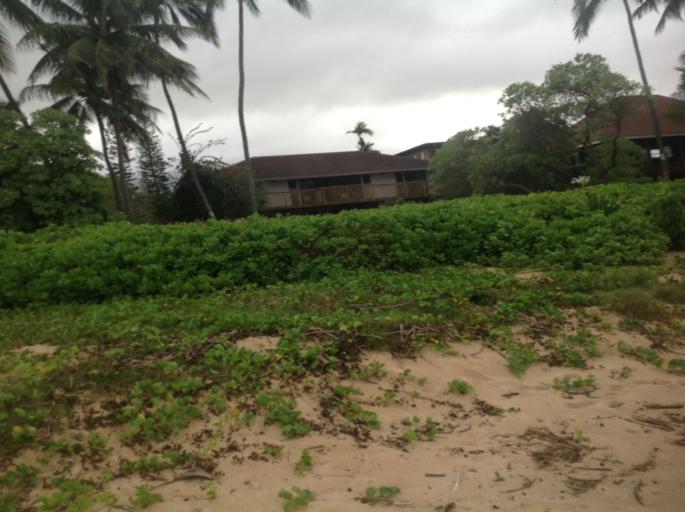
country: US
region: Hawaii
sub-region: Honolulu County
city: Waialua
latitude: 21.5823
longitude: -158.1289
